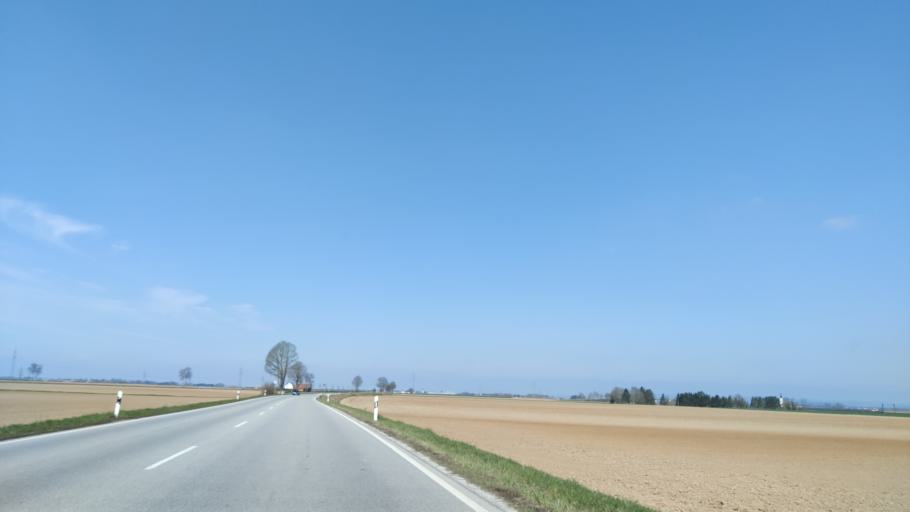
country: DE
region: Bavaria
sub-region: Lower Bavaria
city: Stephansposching
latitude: 48.8058
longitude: 12.7878
